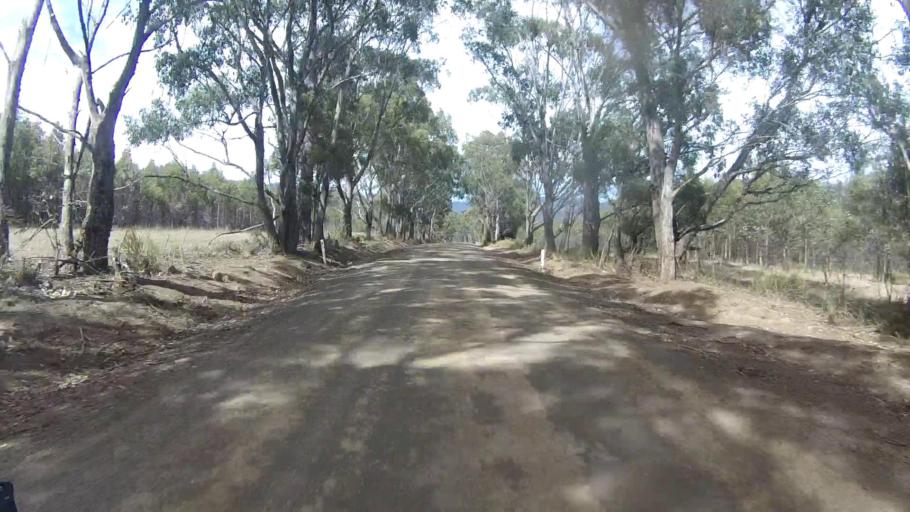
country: AU
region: Tasmania
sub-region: Sorell
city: Sorell
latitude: -42.6599
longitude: 147.8958
